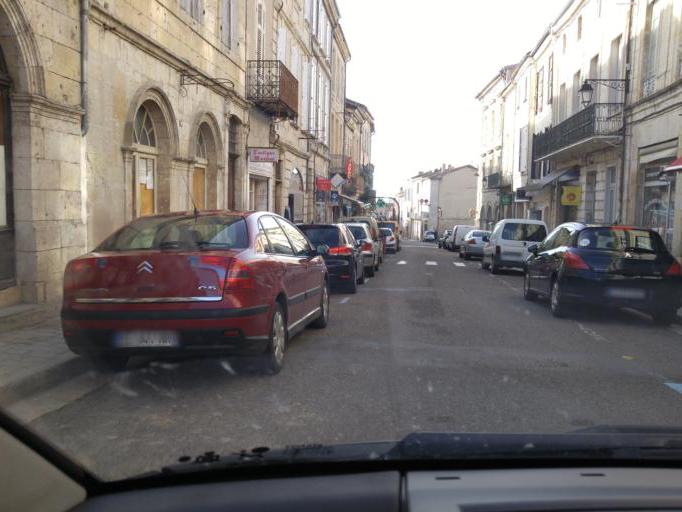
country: FR
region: Midi-Pyrenees
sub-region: Departement du Gers
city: Lectoure
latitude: 43.9344
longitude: 0.6211
